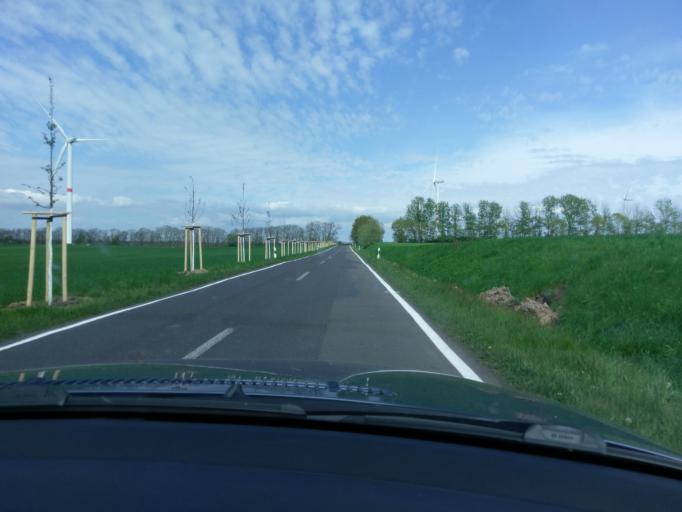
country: DE
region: Brandenburg
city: Eberswalde
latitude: 52.7453
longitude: 13.8520
